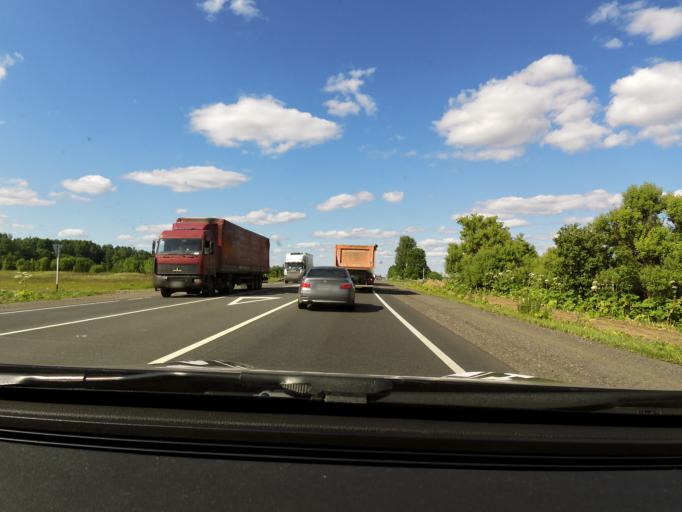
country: RU
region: Novgorod
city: Chudovo
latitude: 58.9627
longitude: 31.5325
